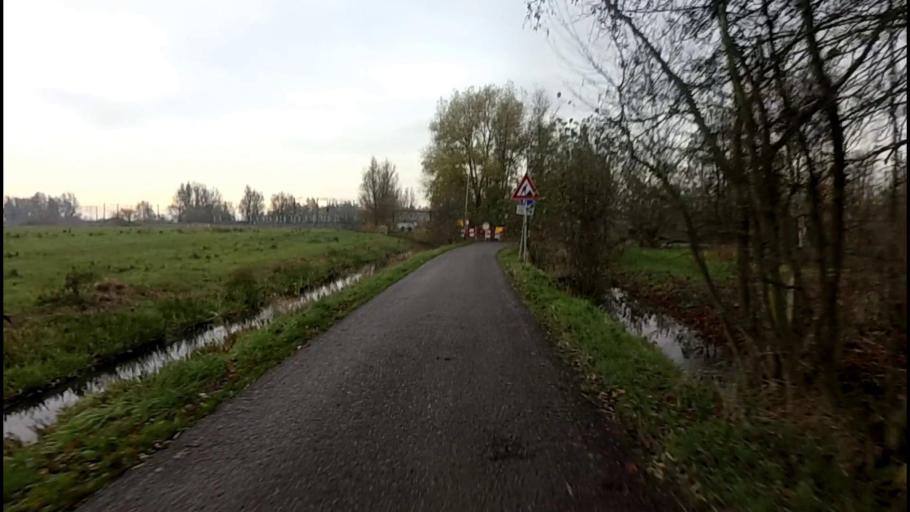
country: NL
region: South Holland
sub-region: Gemeente Vlist
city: Haastrecht
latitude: 52.0156
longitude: 4.7497
